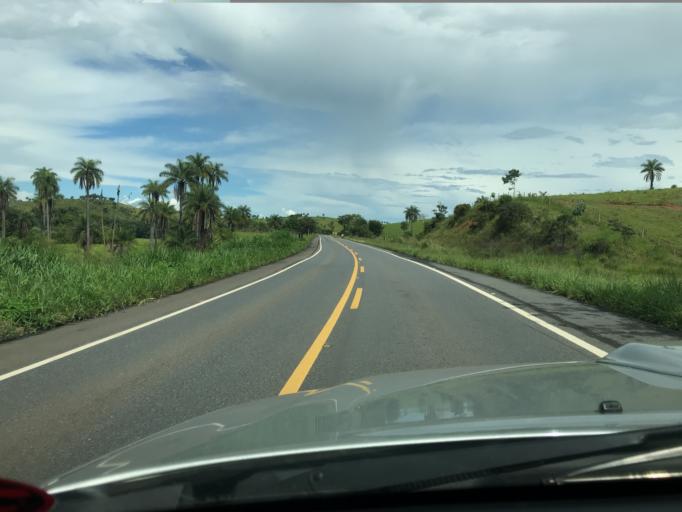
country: BR
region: Minas Gerais
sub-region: Bambui
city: Bambui
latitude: -19.8304
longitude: -46.0086
